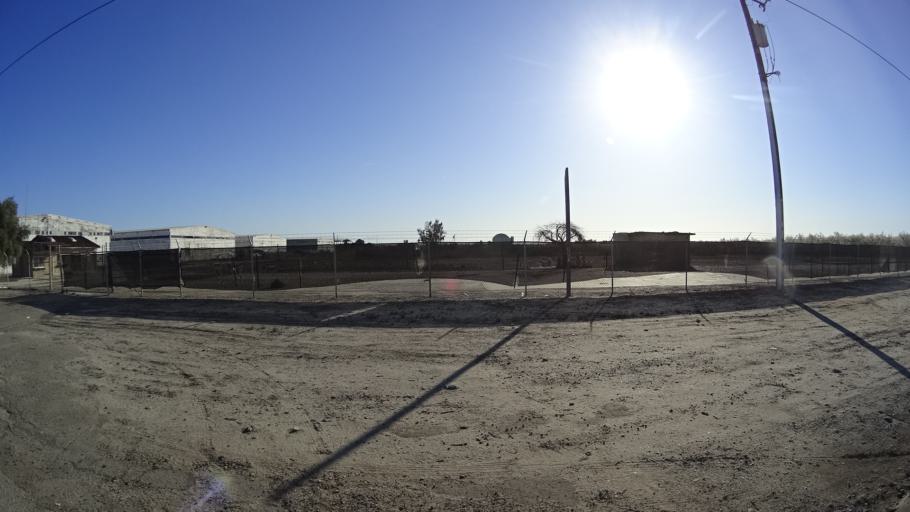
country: US
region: California
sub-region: Fresno County
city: West Park
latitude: 36.7866
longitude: -119.9163
